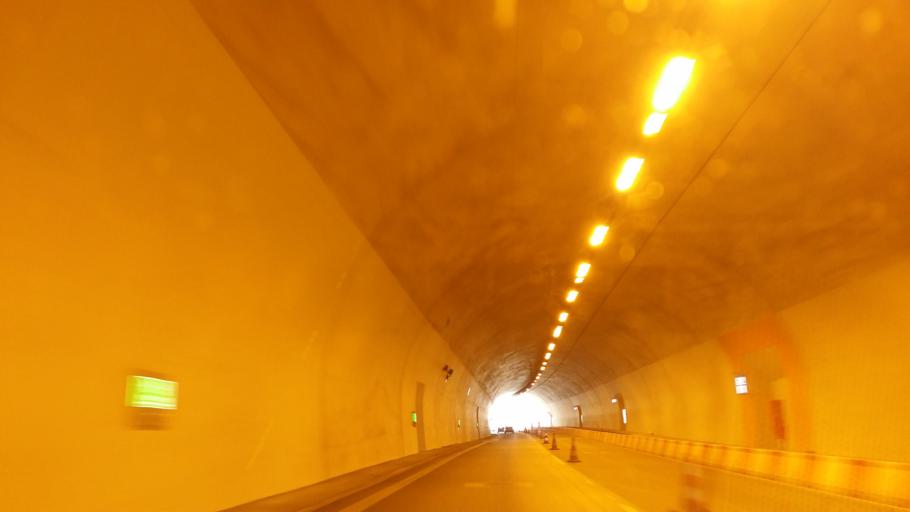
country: GR
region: West Greece
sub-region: Nomos Achaias
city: Aiyira
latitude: 38.1509
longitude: 22.3465
